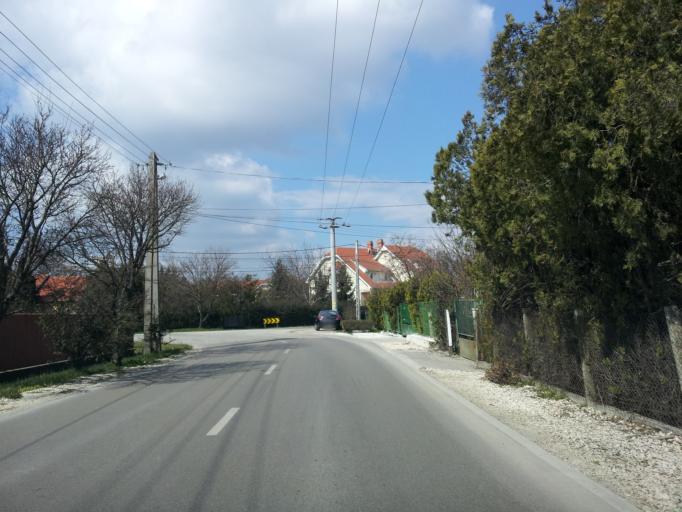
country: HU
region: Pest
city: Toeroekbalint
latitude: 47.4134
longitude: 18.8958
